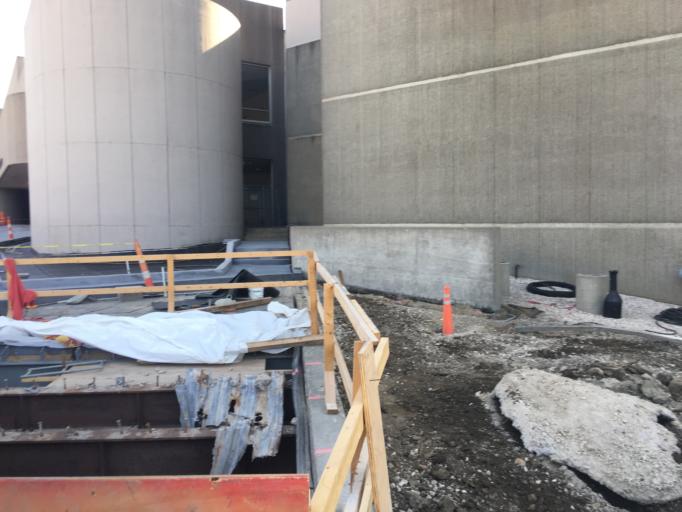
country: US
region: Ohio
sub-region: Franklin County
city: Columbus
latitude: 39.9700
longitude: -83.0021
